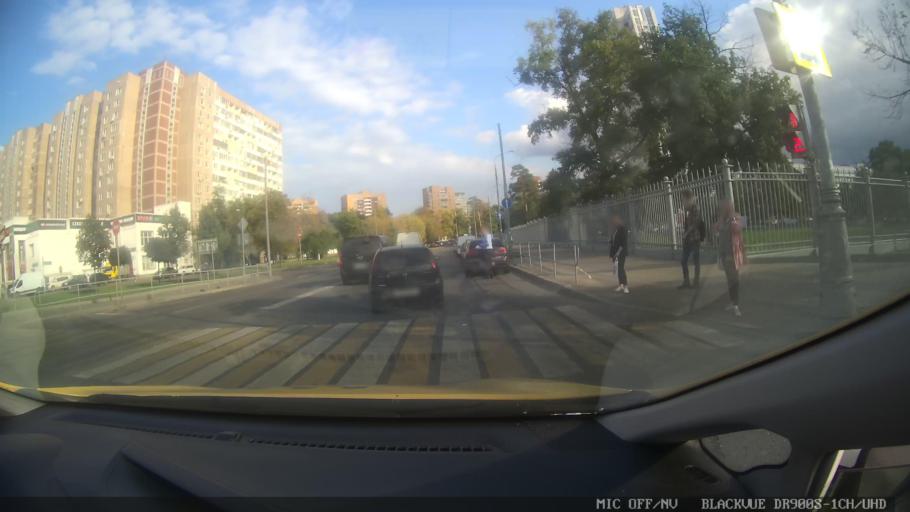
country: RU
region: Moscow
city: Vatutino
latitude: 55.8603
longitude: 37.6922
